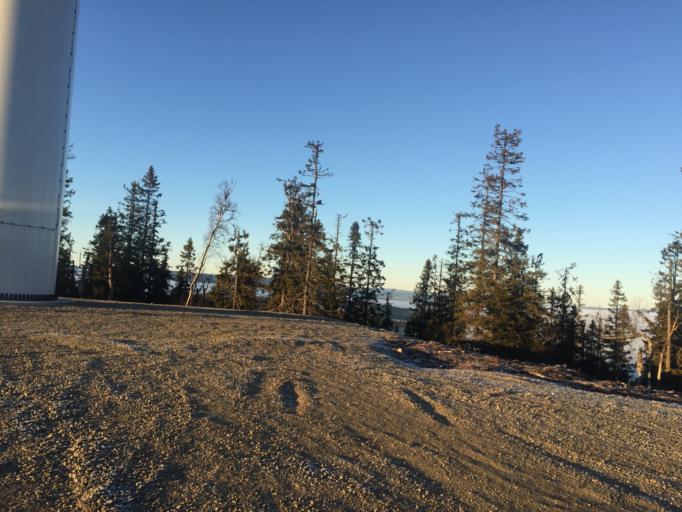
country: NO
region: Hedmark
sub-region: Elverum
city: Elverum
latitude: 61.2138
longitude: 11.7784
